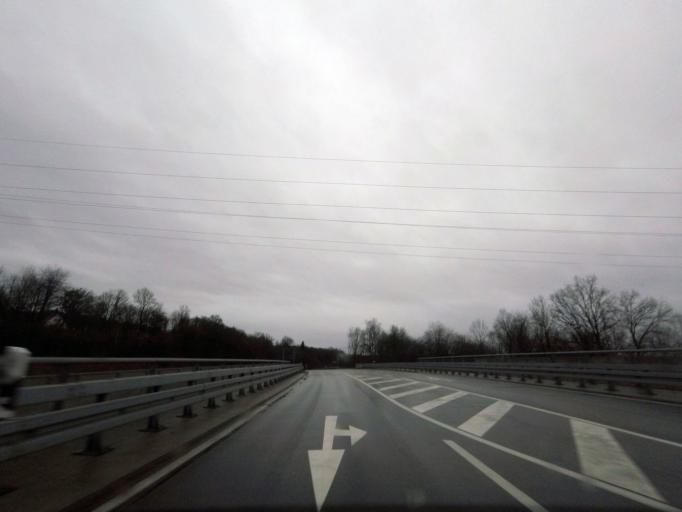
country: DE
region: Baden-Wuerttemberg
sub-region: Regierungsbezirk Stuttgart
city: Backnang
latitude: 48.9399
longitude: 9.4166
